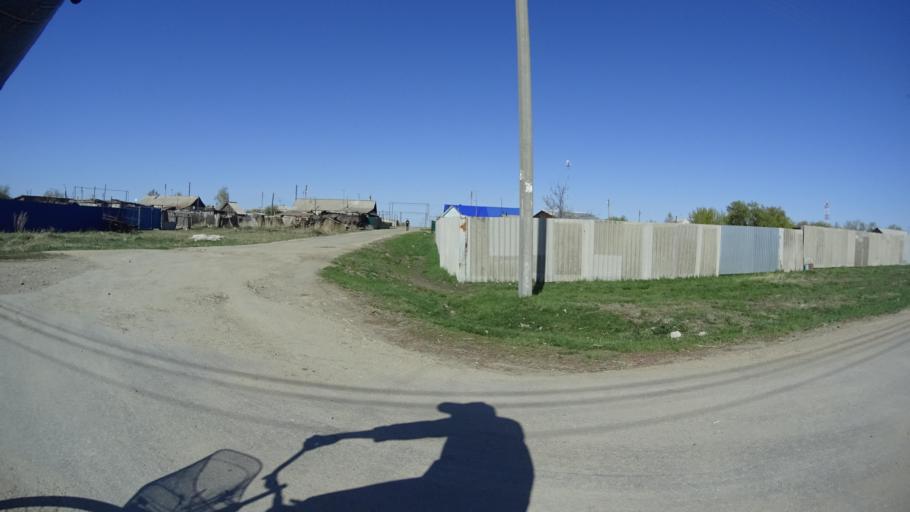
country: RU
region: Chelyabinsk
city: Chesma
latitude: 53.7936
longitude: 61.0326
